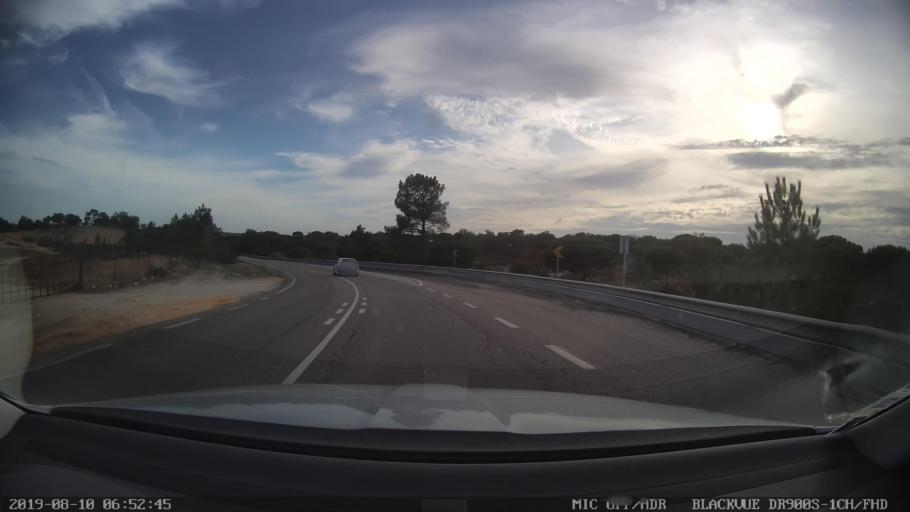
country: PT
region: Santarem
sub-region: Benavente
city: Poceirao
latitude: 38.8772
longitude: -8.7465
